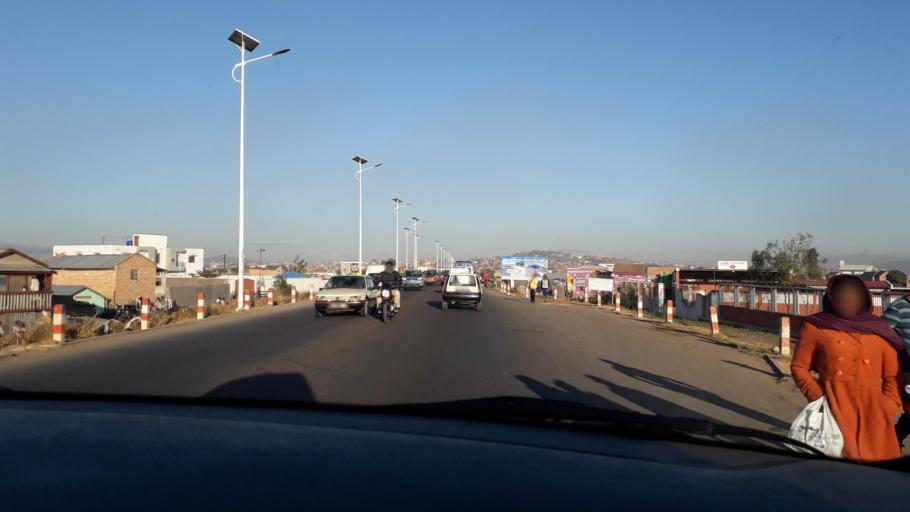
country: MG
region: Analamanga
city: Antananarivo
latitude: -18.8941
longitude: 47.5060
